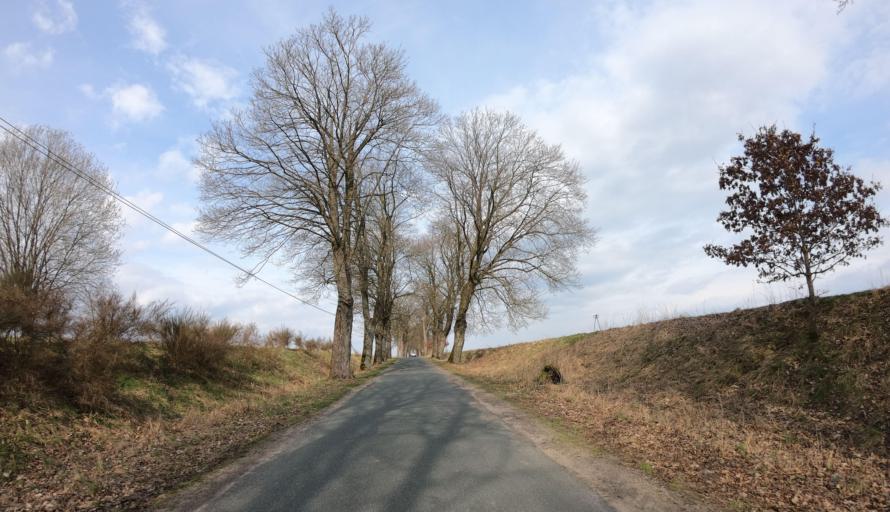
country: PL
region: West Pomeranian Voivodeship
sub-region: Powiat swidwinski
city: Swidwin
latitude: 53.8273
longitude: 15.8260
